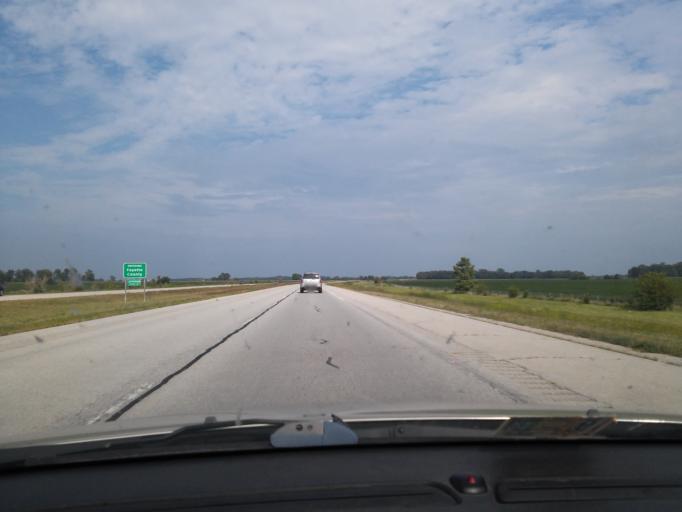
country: US
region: Ohio
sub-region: Greene County
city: Jamestown
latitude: 39.6477
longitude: -83.6613
